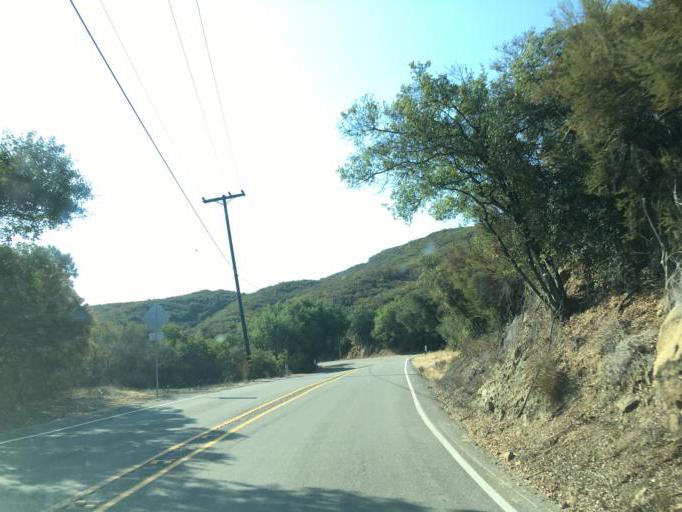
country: US
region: California
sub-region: Los Angeles County
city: Las Flores
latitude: 34.0860
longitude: -118.6575
